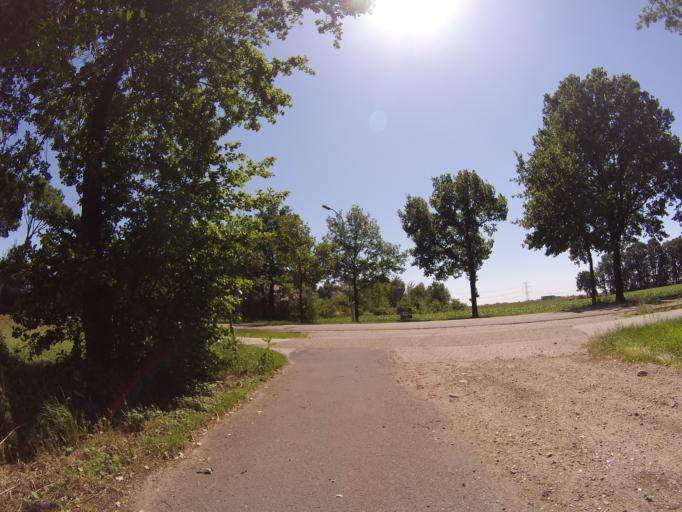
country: NL
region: Drenthe
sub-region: Gemeente Coevorden
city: Sleen
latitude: 52.7608
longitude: 6.8354
